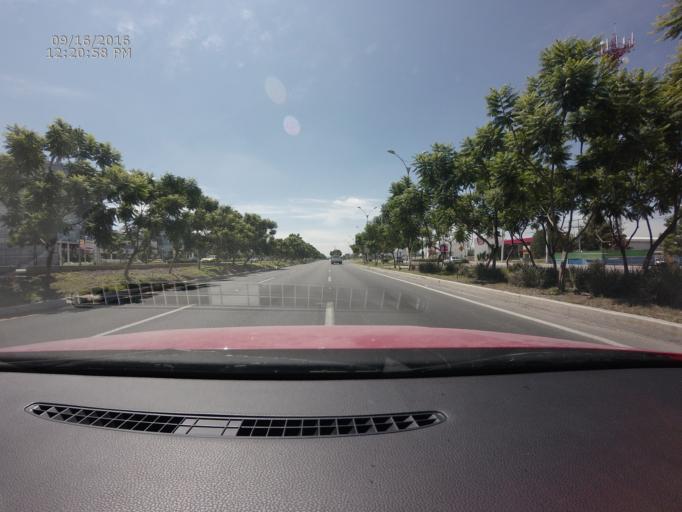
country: MX
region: Queretaro
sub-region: Queretaro
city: El Salitre
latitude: 20.6579
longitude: -100.4324
